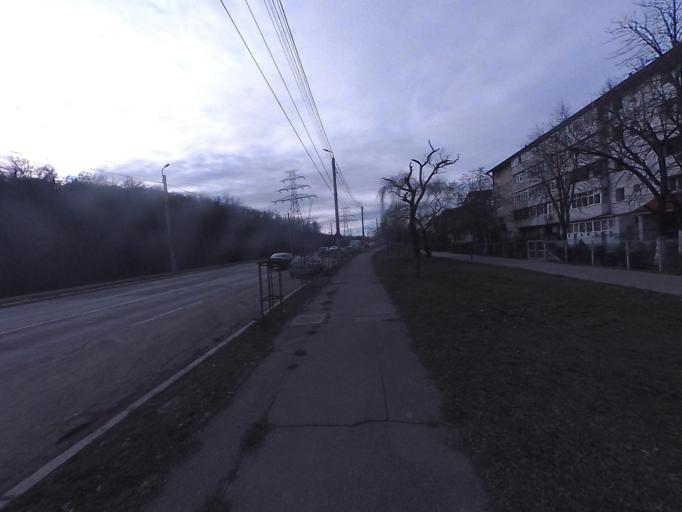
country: RO
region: Iasi
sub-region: Municipiul Iasi
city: Iasi
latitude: 47.1355
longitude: 27.5859
